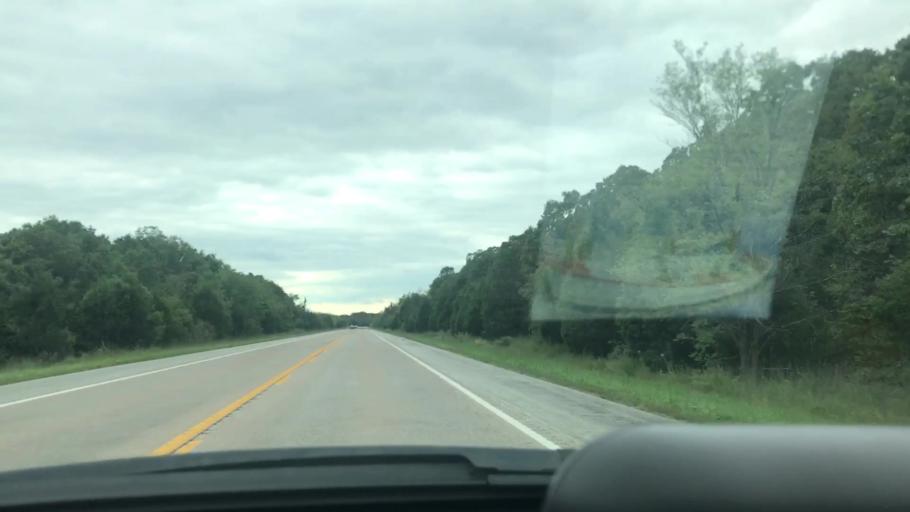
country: US
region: Missouri
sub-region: Benton County
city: Warsaw
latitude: 38.2092
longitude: -93.3333
